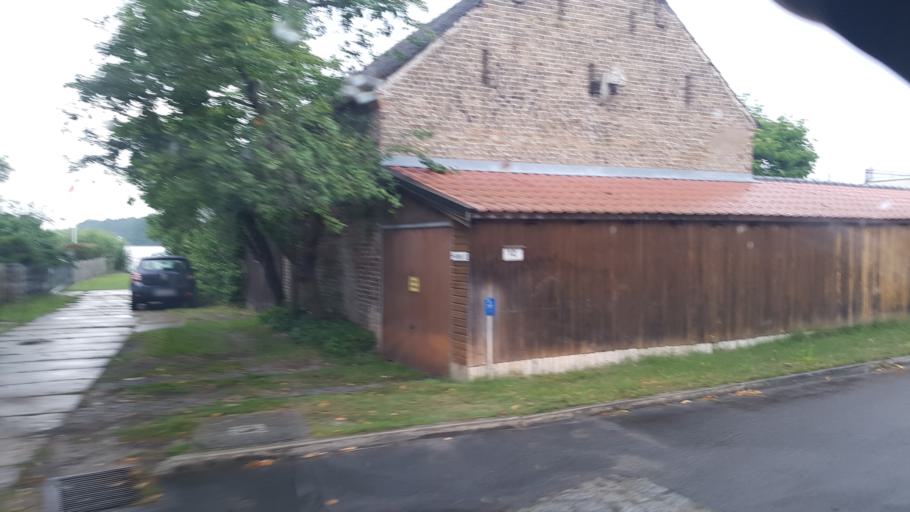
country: DE
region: Brandenburg
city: Gross Koris
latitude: 52.1686
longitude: 13.6864
